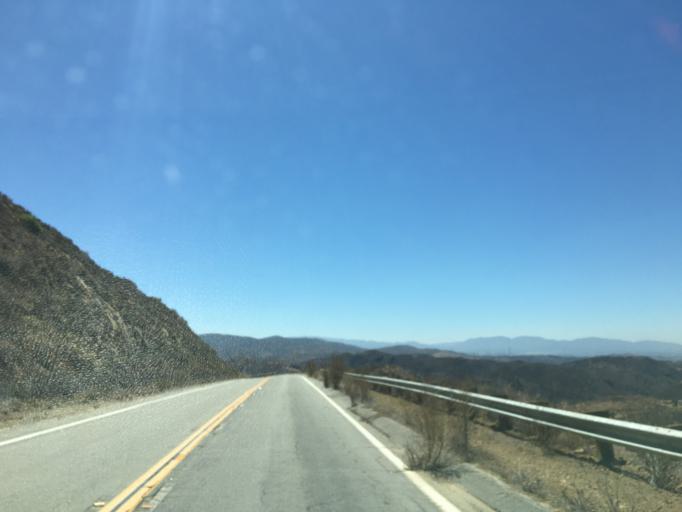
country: US
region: California
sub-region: Los Angeles County
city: Castaic
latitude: 34.5611
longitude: -118.5508
